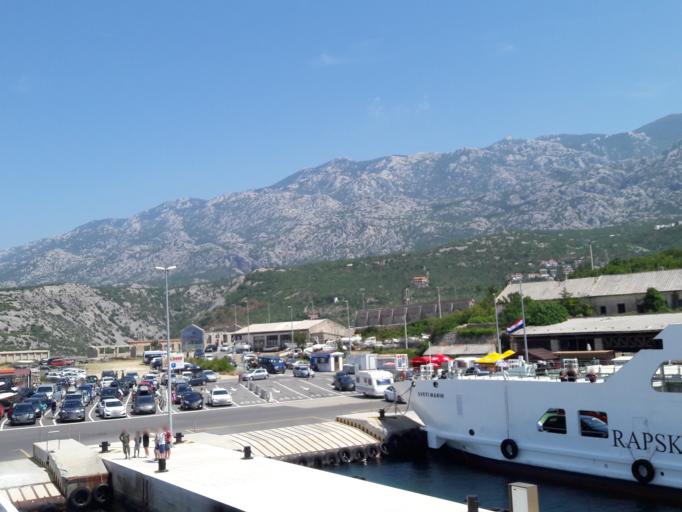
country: HR
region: Primorsko-Goranska
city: Banjol
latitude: 44.7198
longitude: 14.8909
